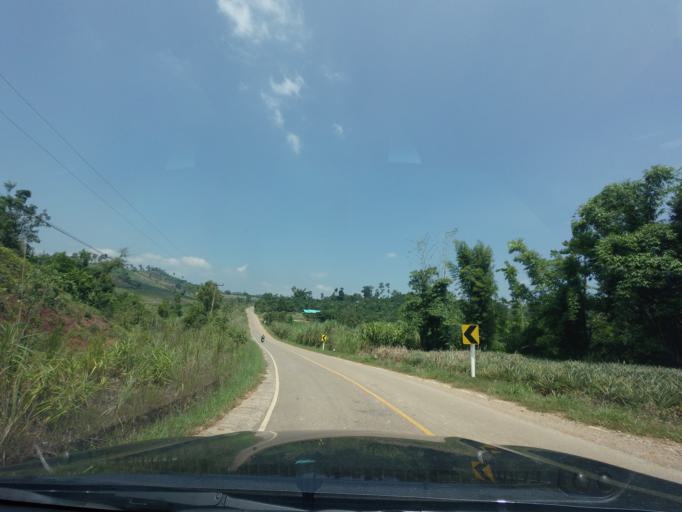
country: TH
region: Loei
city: Na Haeo
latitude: 17.5315
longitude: 100.8800
